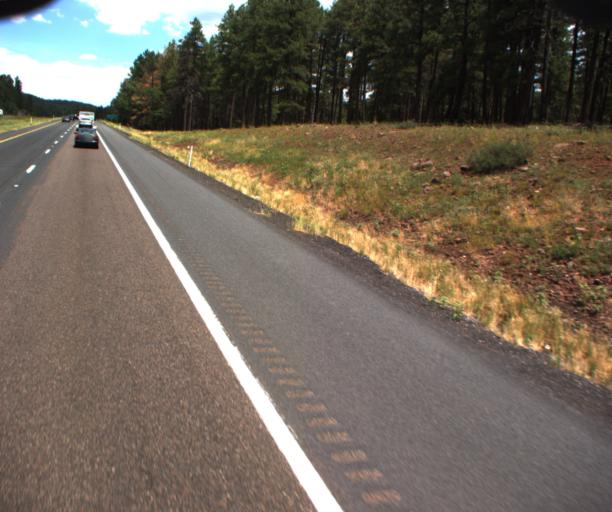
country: US
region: Arizona
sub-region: Coconino County
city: Sedona
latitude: 34.9615
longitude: -111.6798
